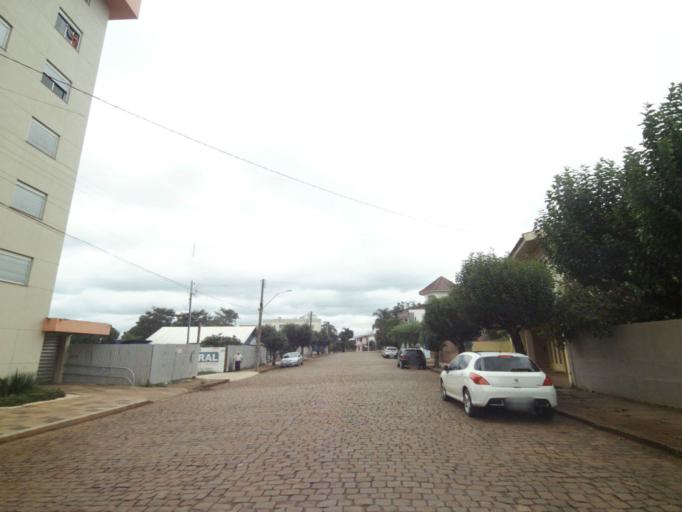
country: BR
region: Rio Grande do Sul
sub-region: Lagoa Vermelha
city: Lagoa Vermelha
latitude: -28.2092
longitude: -51.5198
